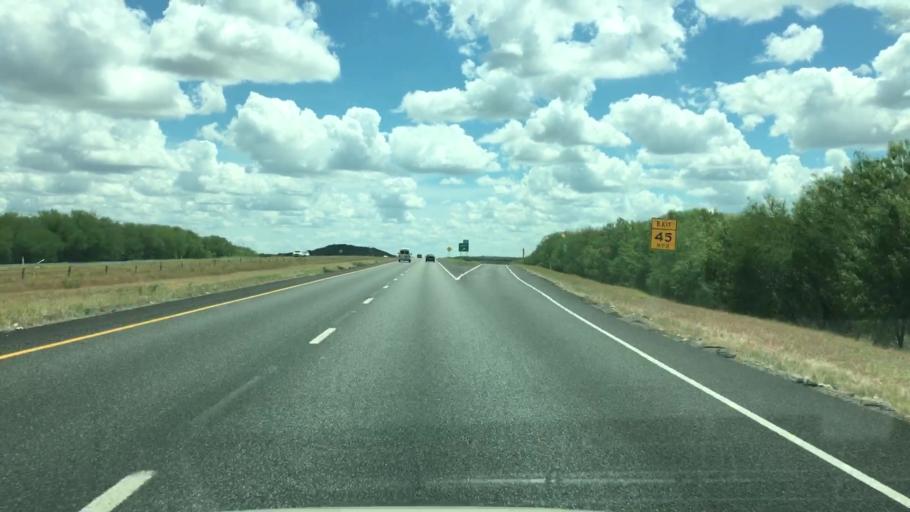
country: US
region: Texas
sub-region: Atascosa County
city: Pleasanton
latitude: 28.7383
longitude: -98.2910
